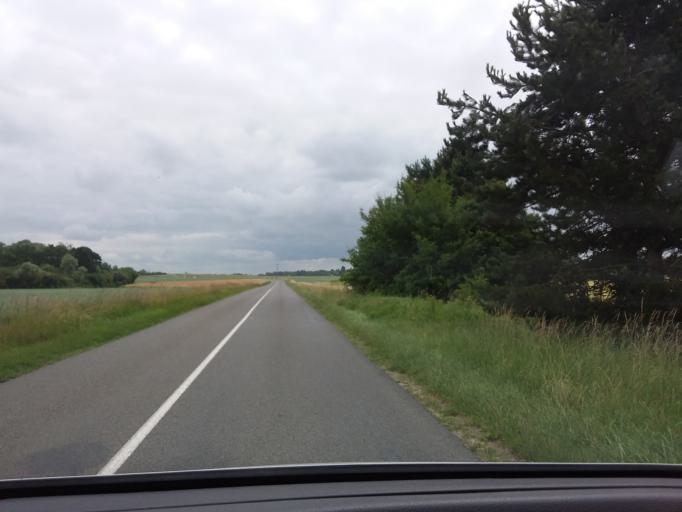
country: FR
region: Champagne-Ardenne
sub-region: Departement de la Marne
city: Cormicy
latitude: 49.4118
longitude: 3.8732
